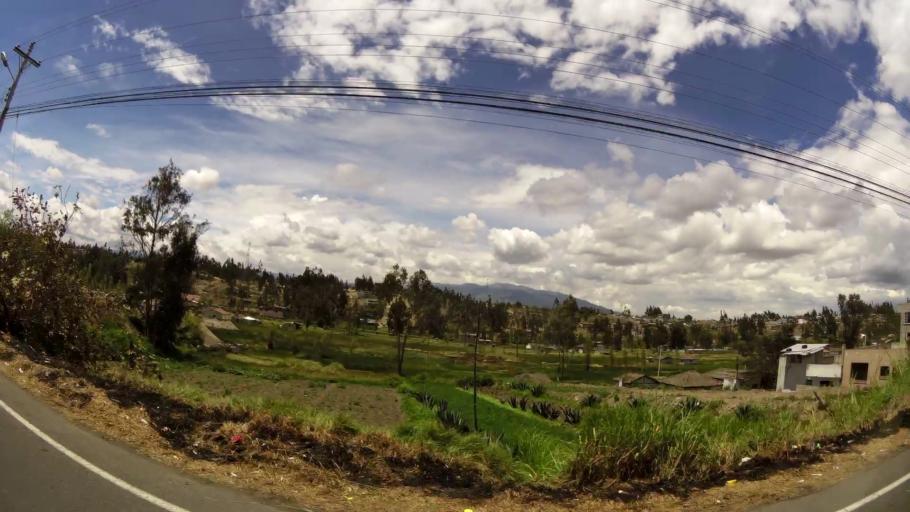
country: EC
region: Tungurahua
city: Ambato
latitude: -1.2800
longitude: -78.5910
